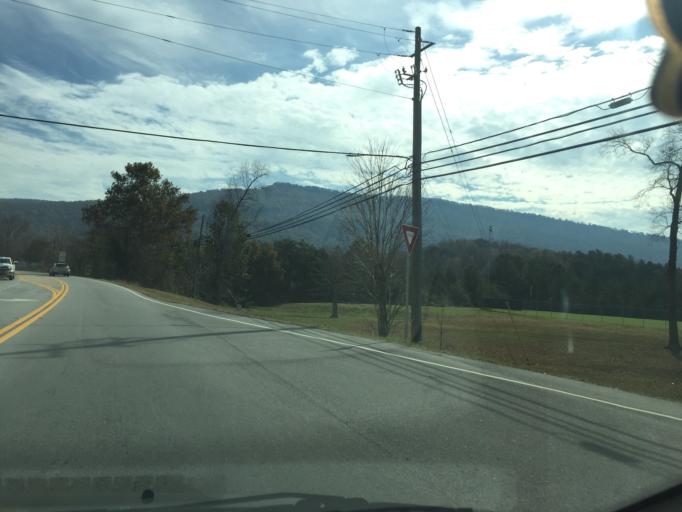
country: US
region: Georgia
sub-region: Dade County
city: Trenton
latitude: 34.8635
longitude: -85.5057
